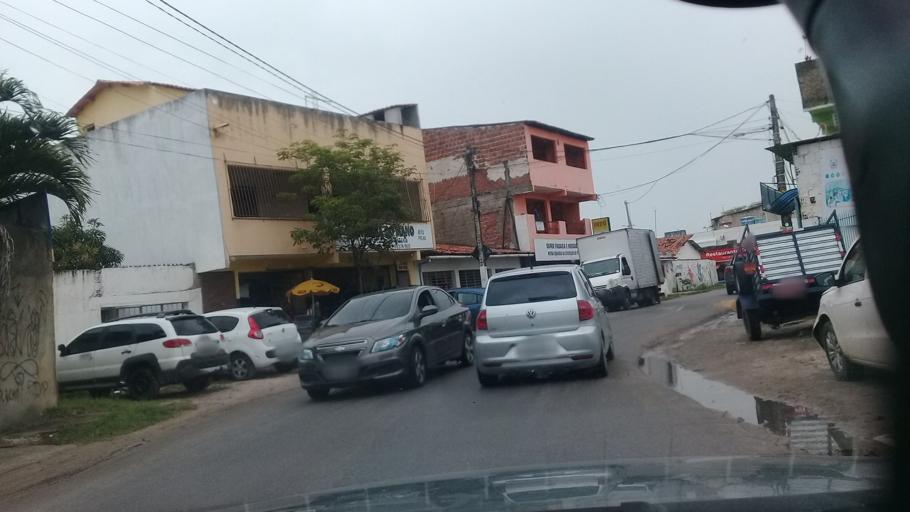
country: BR
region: Pernambuco
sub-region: Itamaraca
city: Itamaraca
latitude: -7.7436
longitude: -34.8243
